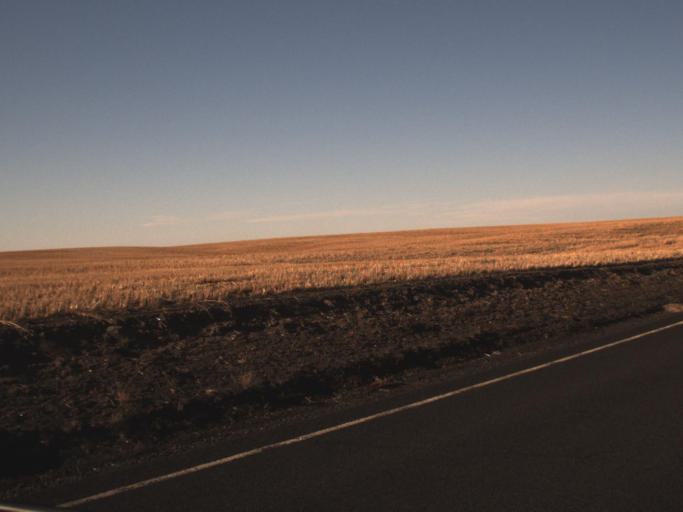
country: US
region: Washington
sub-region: Adams County
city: Ritzville
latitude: 46.8993
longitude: -118.3332
